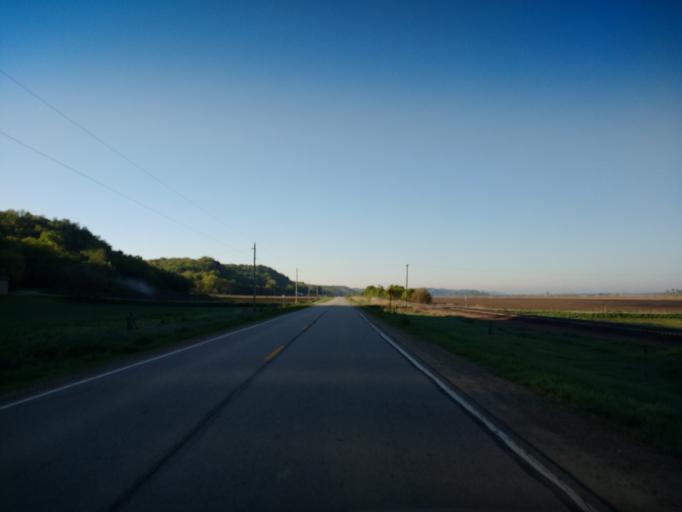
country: US
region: Iowa
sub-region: Harrison County
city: Missouri Valley
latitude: 41.4698
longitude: -95.8800
